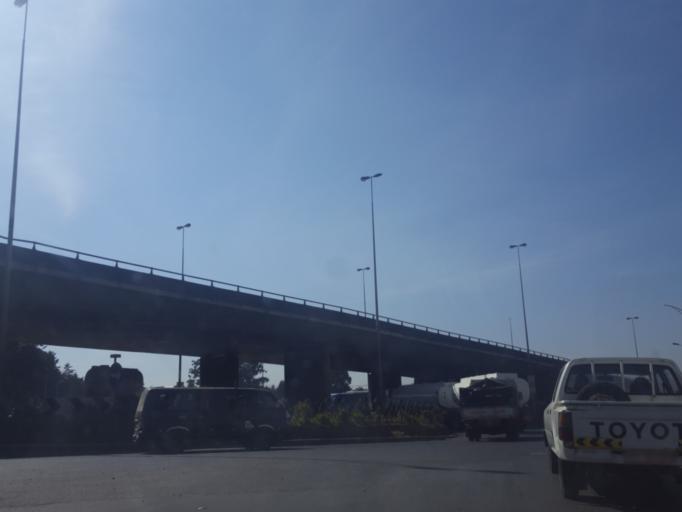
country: ET
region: Adis Abeba
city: Addis Ababa
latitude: 9.0573
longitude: 38.7132
